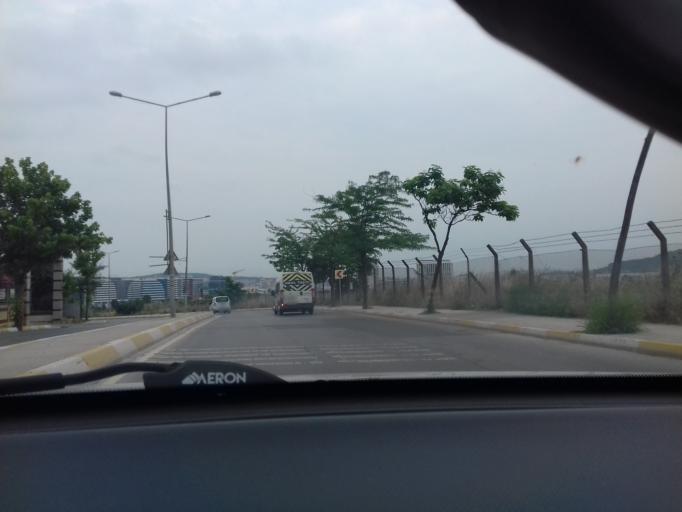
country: TR
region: Istanbul
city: Pendik
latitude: 40.9183
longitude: 29.3078
